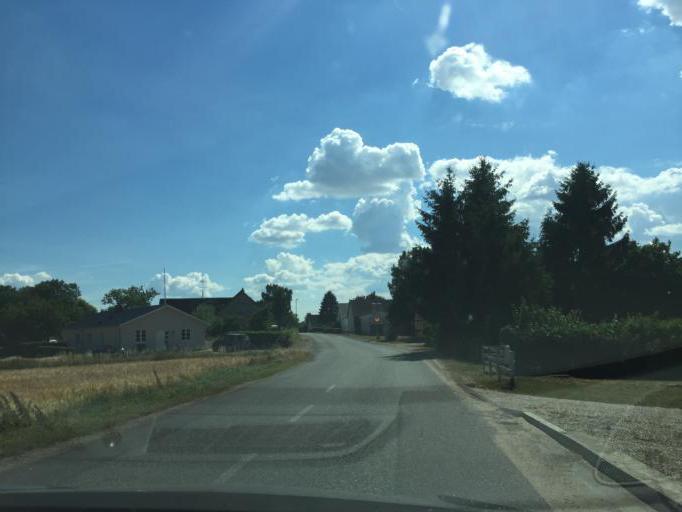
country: DK
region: South Denmark
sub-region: Odense Kommune
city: Bellinge
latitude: 55.2881
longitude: 10.3358
